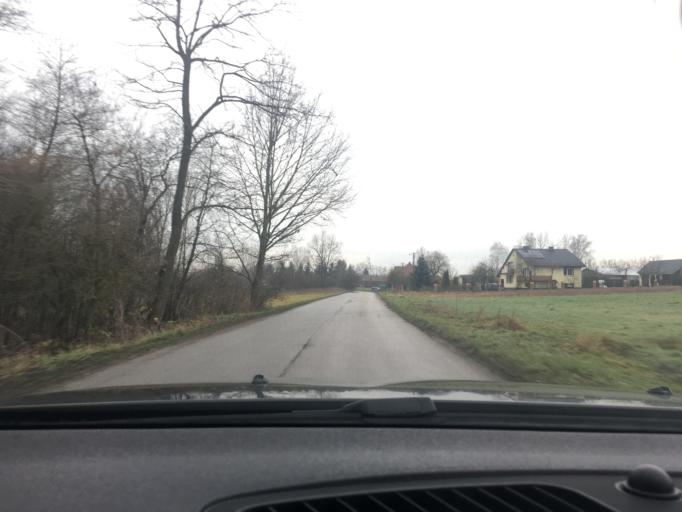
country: PL
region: Swietokrzyskie
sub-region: Powiat jedrzejowski
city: Imielno
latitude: 50.6412
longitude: 20.4089
